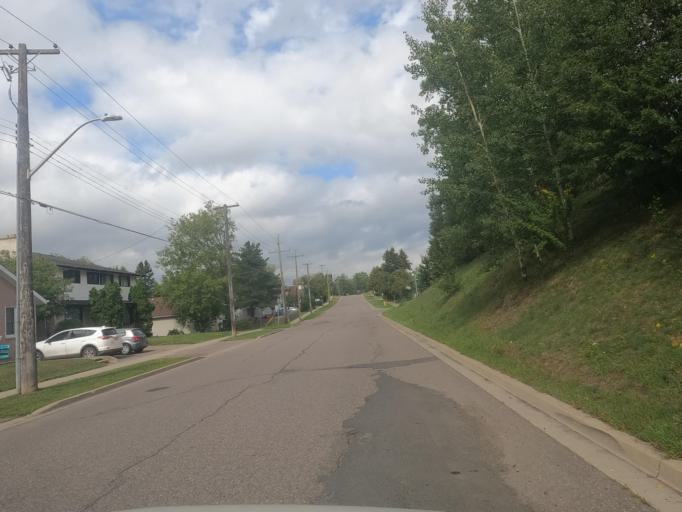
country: CA
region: Ontario
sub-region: Thunder Bay District
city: Thunder Bay
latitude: 48.4420
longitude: -89.2426
